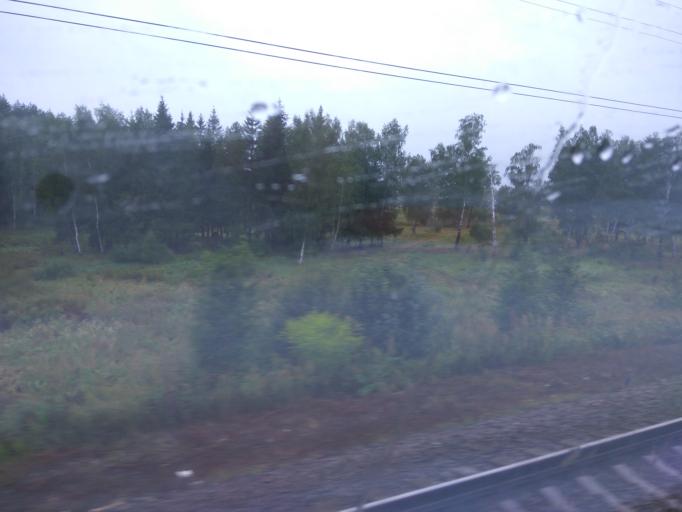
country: RU
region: Moskovskaya
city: Zhilevo
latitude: 54.9771
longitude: 38.0357
